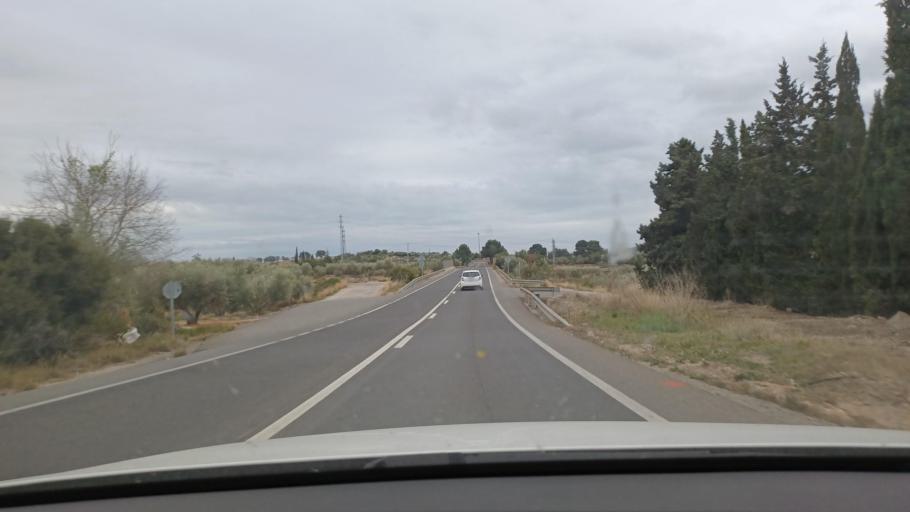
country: ES
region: Catalonia
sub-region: Provincia de Tarragona
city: Masdenverge
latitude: 40.7077
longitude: 0.5460
